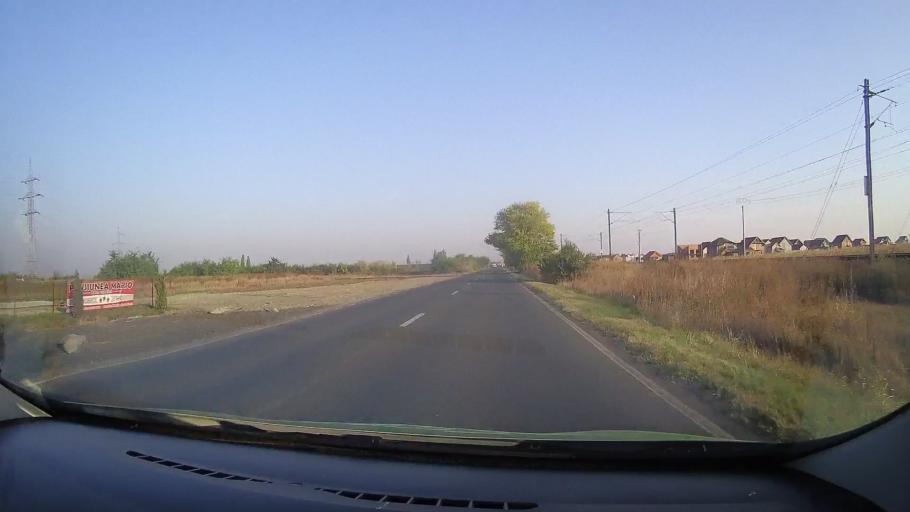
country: RO
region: Arad
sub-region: Comuna Curtici
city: Curtici
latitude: 46.3239
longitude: 21.3061
